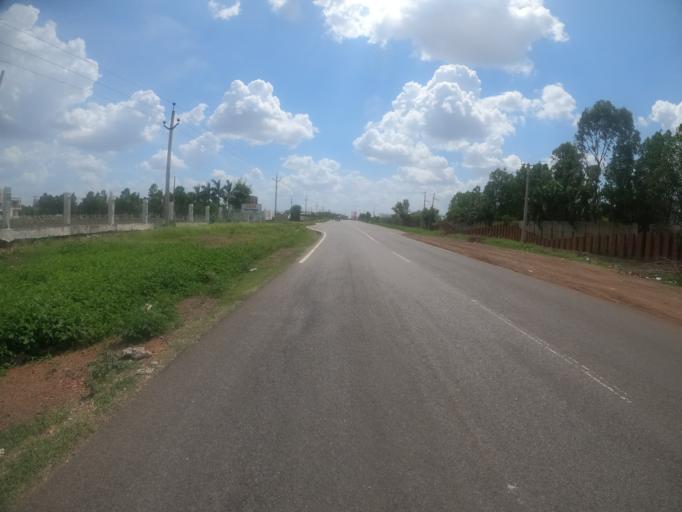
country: IN
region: Telangana
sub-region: Rangareddi
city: Sriramnagar
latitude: 17.3050
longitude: 78.1528
